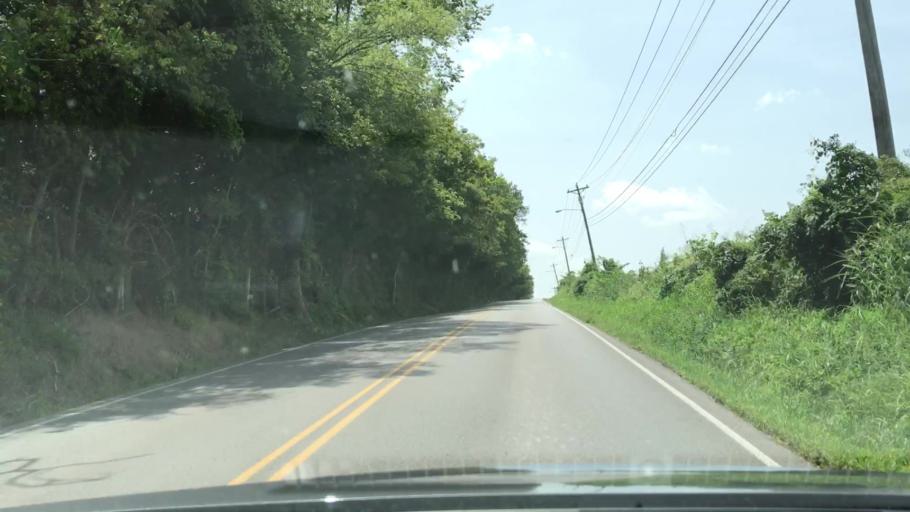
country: US
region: Tennessee
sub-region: Rutherford County
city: La Vergne
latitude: 35.9711
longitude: -86.6001
